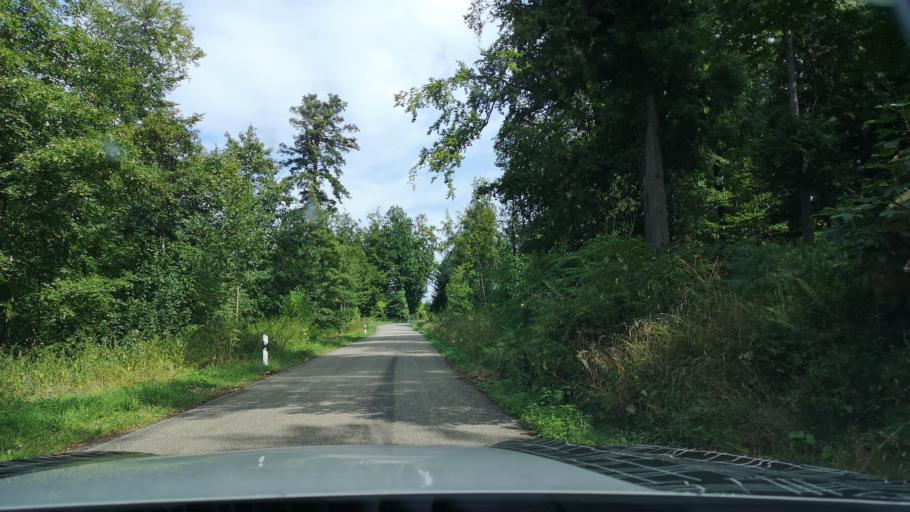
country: DE
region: Baden-Wuerttemberg
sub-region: Karlsruhe Region
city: Bad Herrenalb
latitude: 48.8453
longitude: 8.4435
